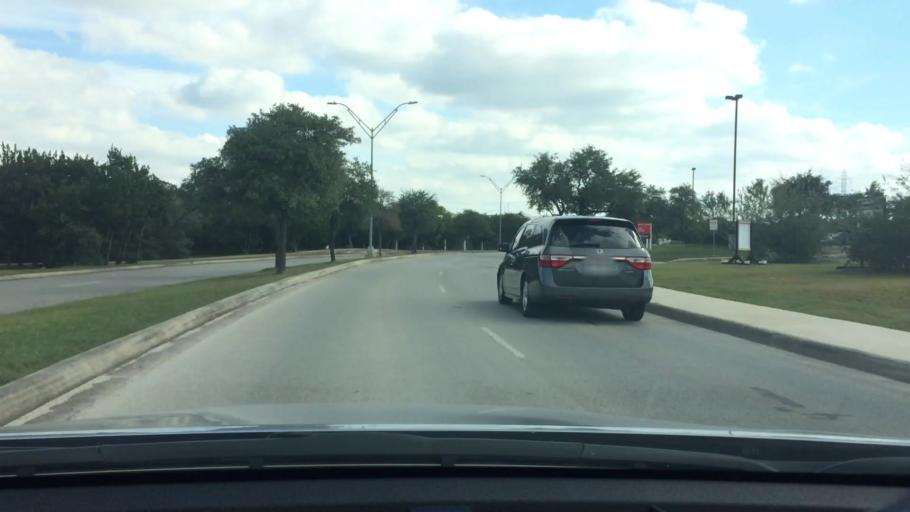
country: US
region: Texas
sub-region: Bexar County
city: Shavano Park
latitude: 29.5806
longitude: -98.5666
